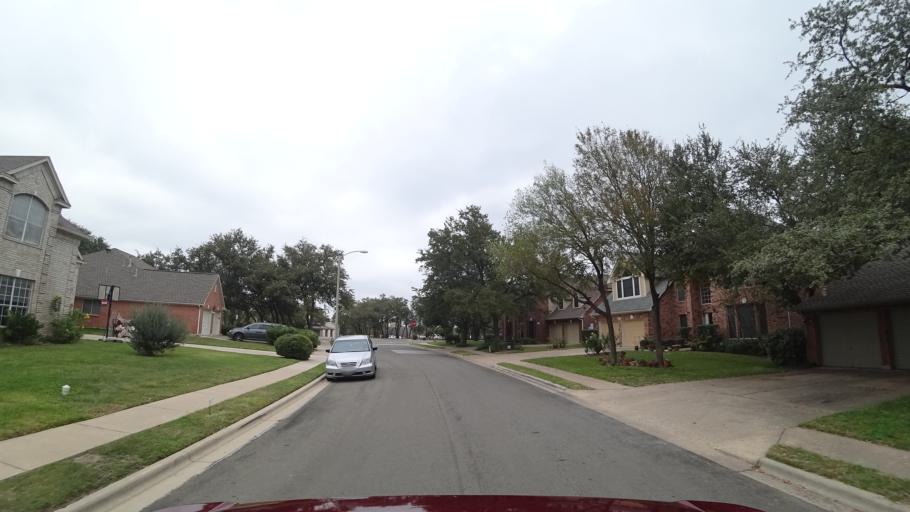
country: US
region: Texas
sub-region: Williamson County
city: Anderson Mill
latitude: 30.4358
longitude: -97.8248
